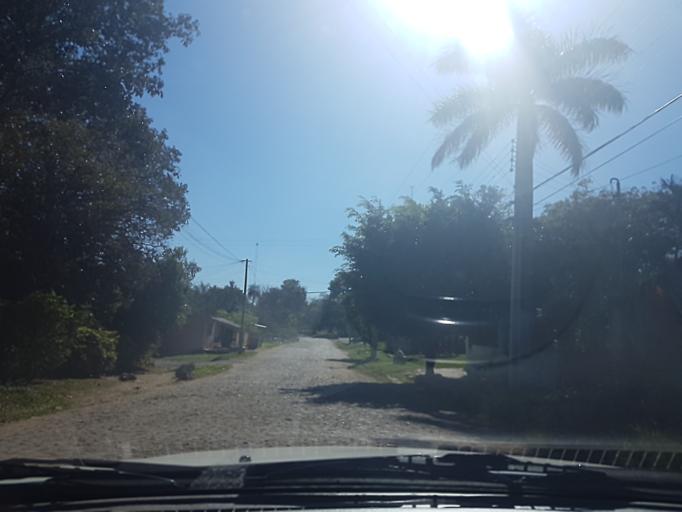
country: PY
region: Central
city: Colonia Mariano Roque Alonso
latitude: -25.2139
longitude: -57.5488
